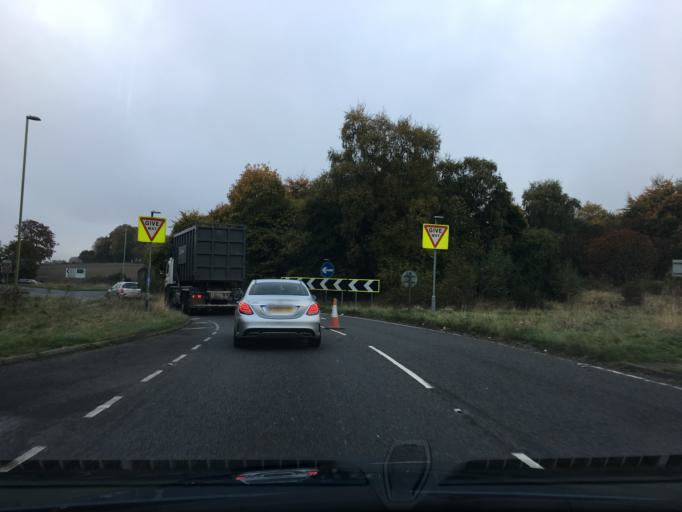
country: GB
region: England
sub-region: Hampshire
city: Alton
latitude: 51.1328
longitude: -0.9938
